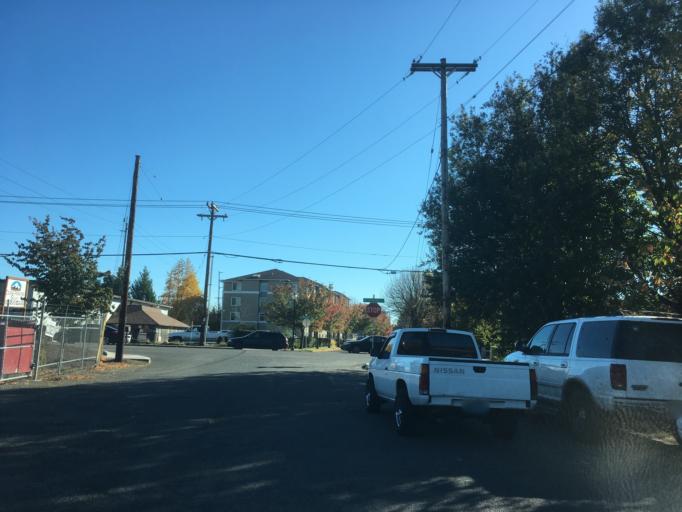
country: US
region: Oregon
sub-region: Multnomah County
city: Gresham
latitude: 45.5017
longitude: -122.4217
